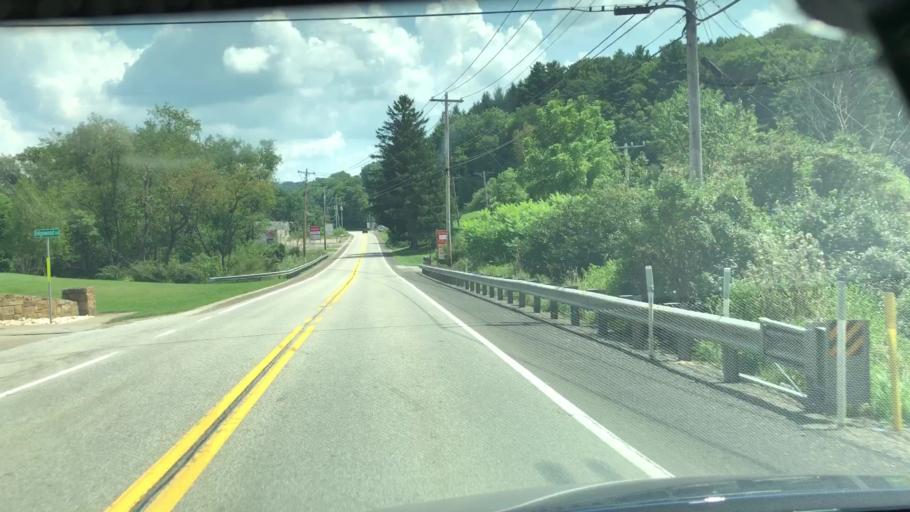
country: US
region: Pennsylvania
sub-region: Armstrong County
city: Freeport
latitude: 40.7138
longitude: -79.7474
